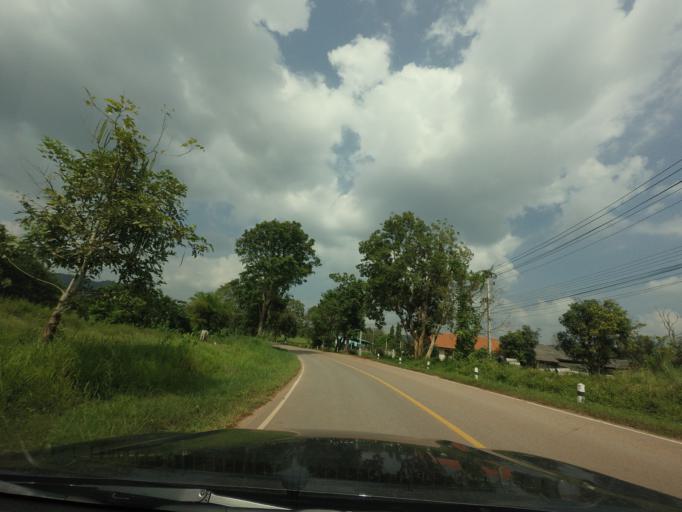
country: TH
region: Uttaradit
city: Ban Khok
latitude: 18.0402
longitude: 101.1031
